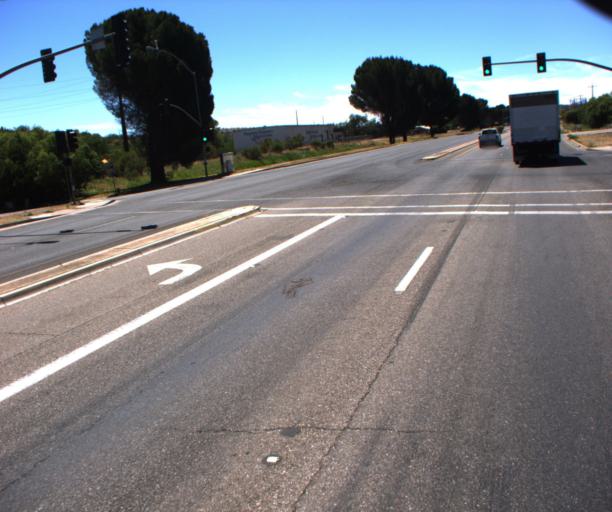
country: US
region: Arizona
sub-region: Santa Cruz County
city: Nogales
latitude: 31.3900
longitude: -110.9527
